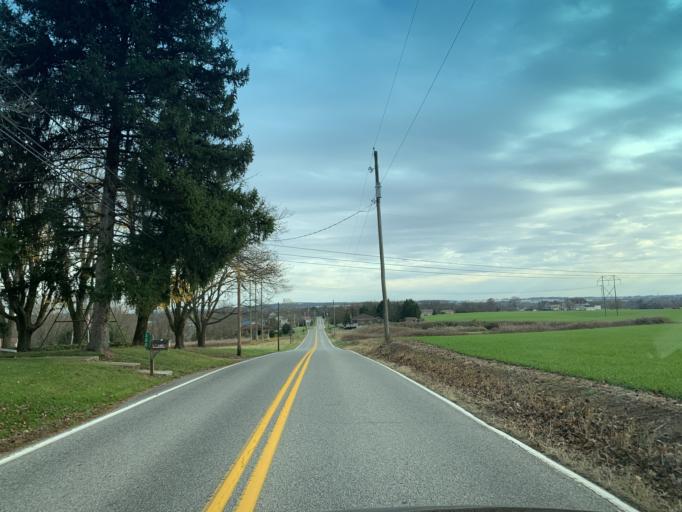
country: US
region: Pennsylvania
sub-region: York County
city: Manchester
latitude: 40.0854
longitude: -76.7530
